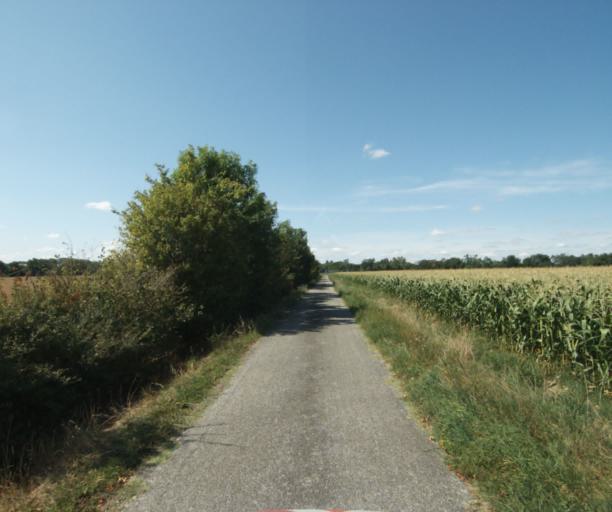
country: FR
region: Midi-Pyrenees
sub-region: Departement de la Haute-Garonne
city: Revel
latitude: 43.4860
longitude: 1.9742
